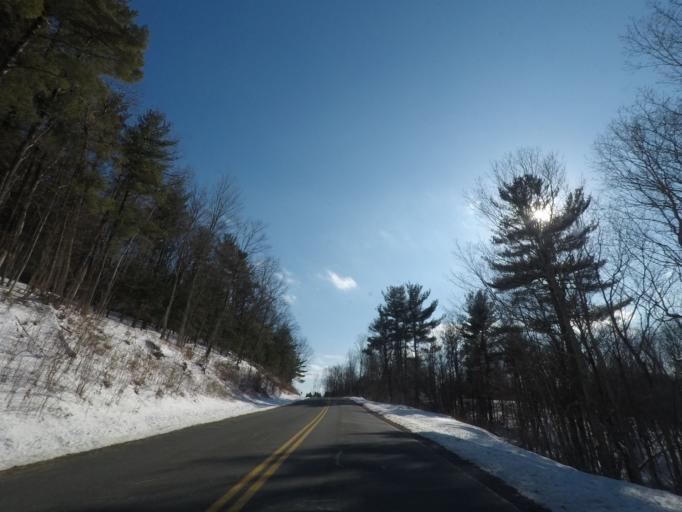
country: US
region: New York
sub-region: Rensselaer County
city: Hoosick Falls
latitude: 42.8885
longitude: -73.4959
